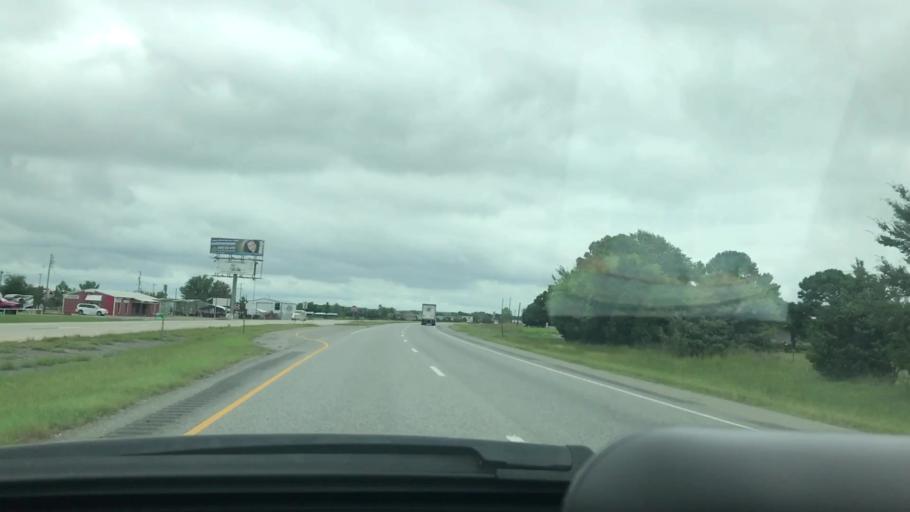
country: US
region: Oklahoma
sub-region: Pittsburg County
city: McAlester
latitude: 34.7317
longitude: -95.8994
